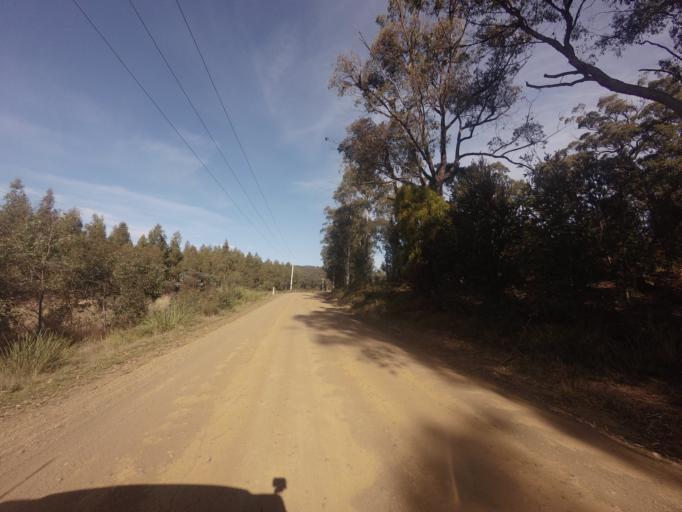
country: AU
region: Tasmania
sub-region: Sorell
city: Sorell
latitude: -42.4952
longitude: 147.5275
